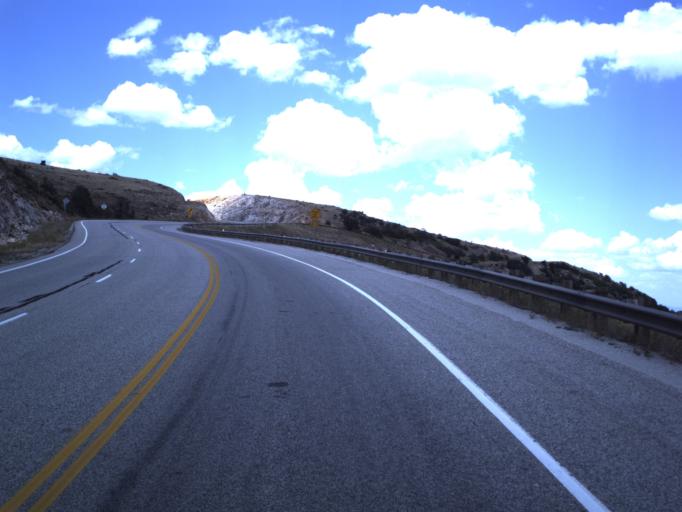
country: US
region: Idaho
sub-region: Bear Lake County
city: Paris
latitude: 41.9278
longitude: -111.4330
